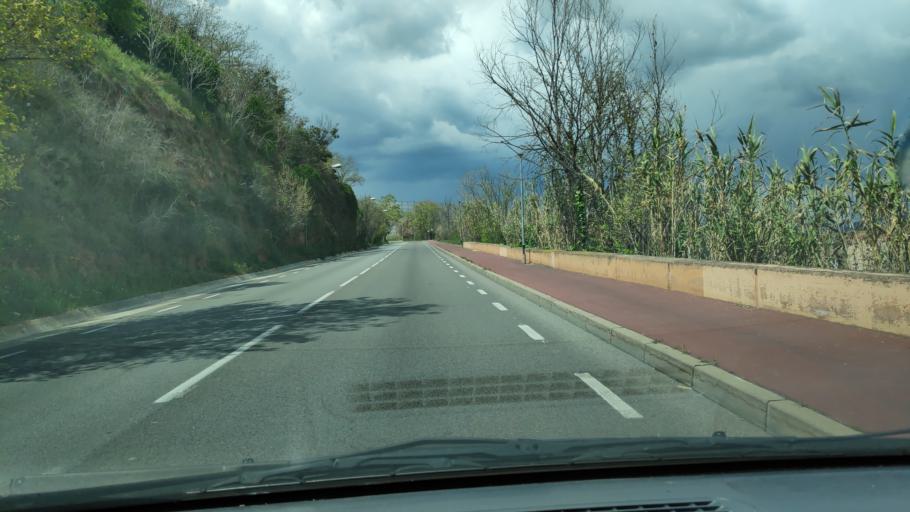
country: ES
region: Catalonia
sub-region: Provincia de Barcelona
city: Sabadell
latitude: 41.5443
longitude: 2.1217
